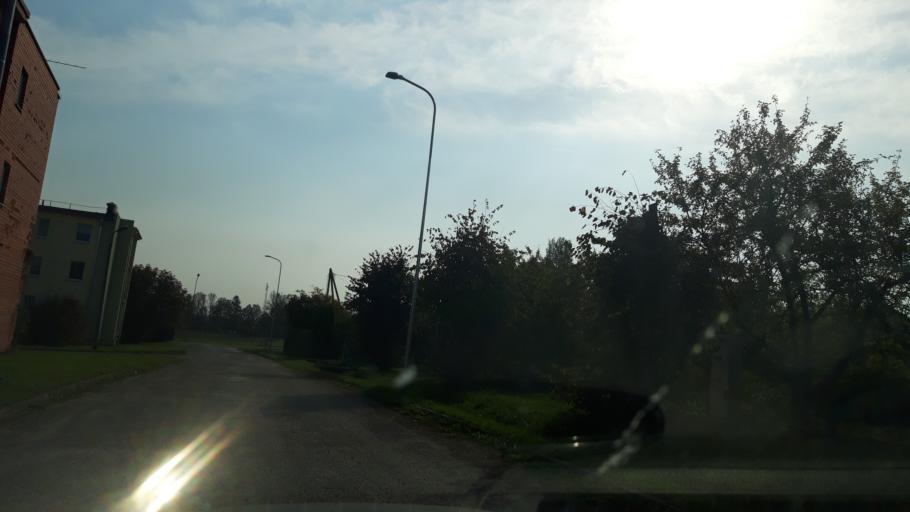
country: LV
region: Mazsalaca
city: Mazsalaca
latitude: 57.8567
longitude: 25.0426
